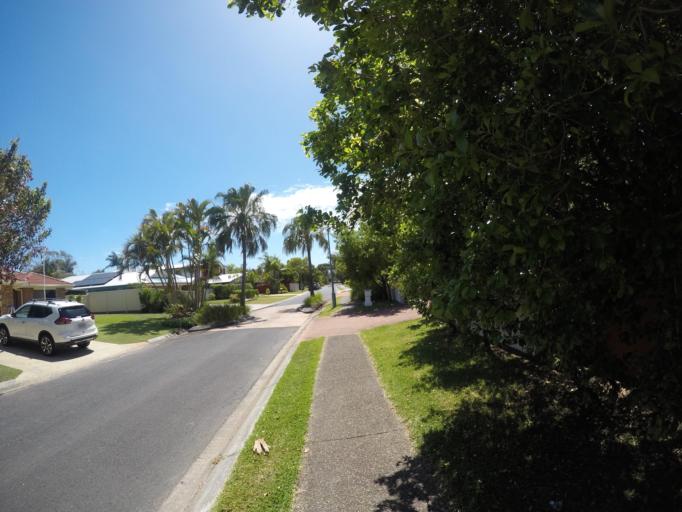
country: AU
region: Queensland
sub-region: Sunshine Coast
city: Mooloolaba
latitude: -26.6136
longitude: 153.0941
